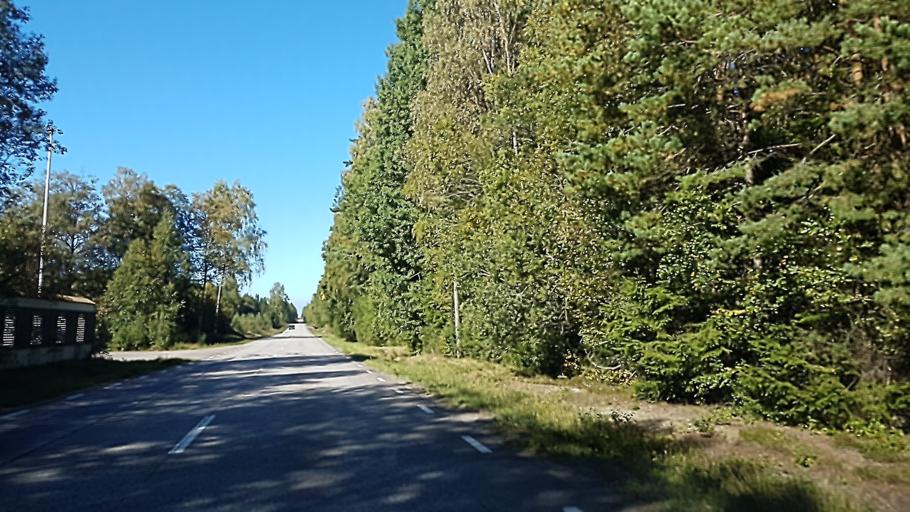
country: SE
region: Kronoberg
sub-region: Ljungby Kommun
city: Ljungby
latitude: 56.8259
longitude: 14.0470
